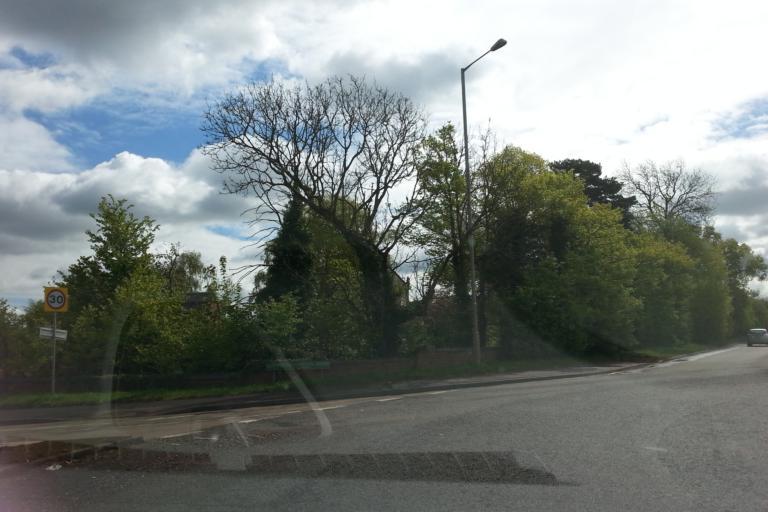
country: GB
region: England
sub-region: Staffordshire
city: Essington
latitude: 52.6534
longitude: -2.0533
